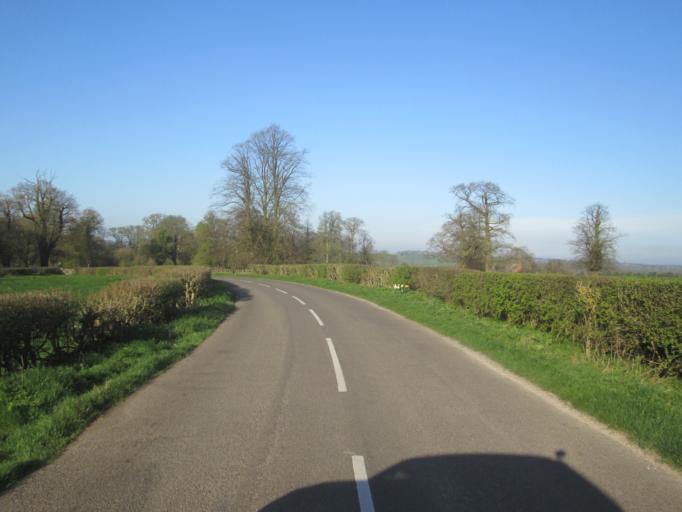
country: GB
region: England
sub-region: Derbyshire
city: Duffield
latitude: 52.9708
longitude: -1.5298
